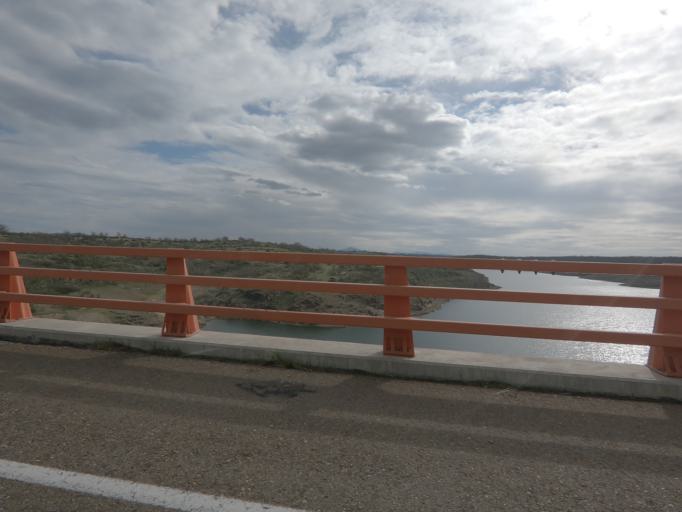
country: ES
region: Castille and Leon
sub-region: Provincia de Salamanca
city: Robleda
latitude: 40.4291
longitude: -6.6011
